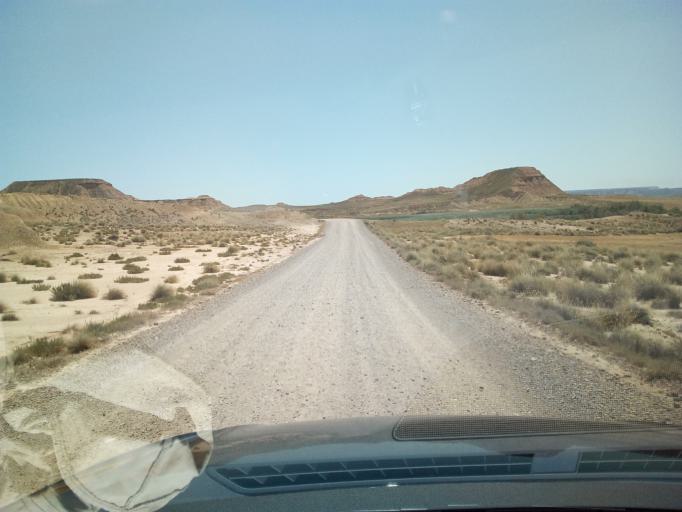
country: ES
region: Navarre
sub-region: Provincia de Navarra
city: Arguedas
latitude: 42.2076
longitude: -1.5103
